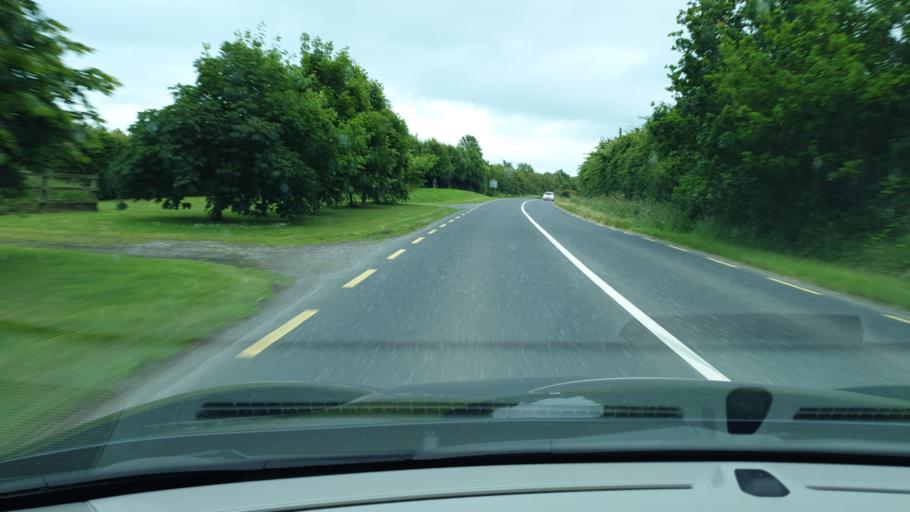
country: IE
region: Leinster
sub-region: An Mhi
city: Dunshaughlin
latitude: 53.4657
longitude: -6.5311
